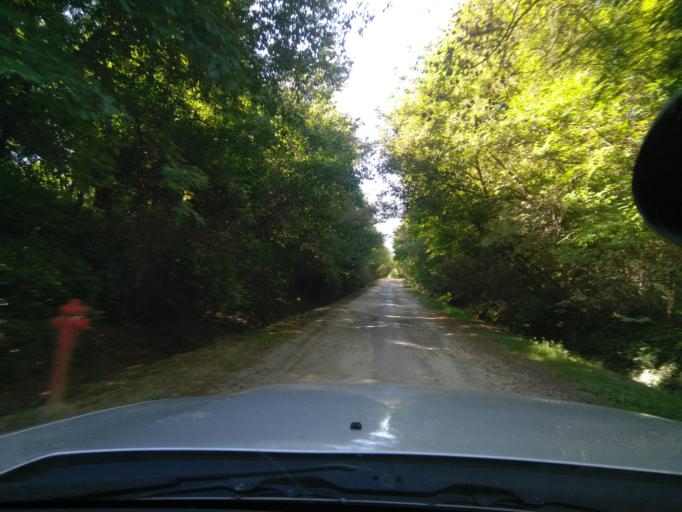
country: HU
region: Fejer
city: Baracska
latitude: 47.3176
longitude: 18.7176
